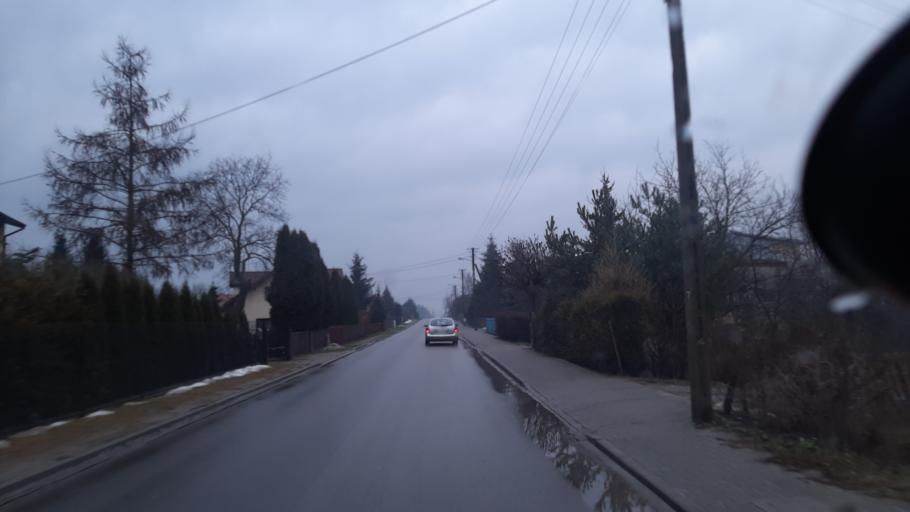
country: PL
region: Lublin Voivodeship
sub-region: Powiat lubartowski
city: Serniki
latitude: 51.4390
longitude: 22.6562
